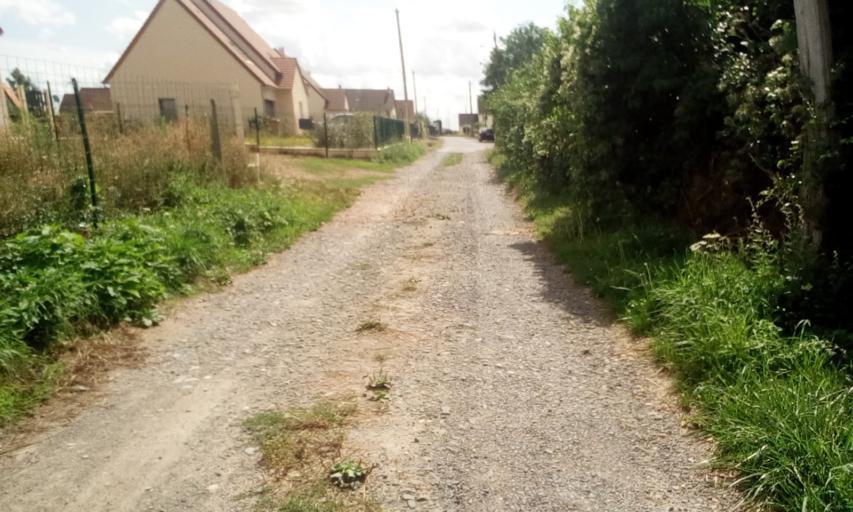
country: FR
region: Lower Normandy
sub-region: Departement du Calvados
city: Bellengreville
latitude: 49.1098
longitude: -0.2106
